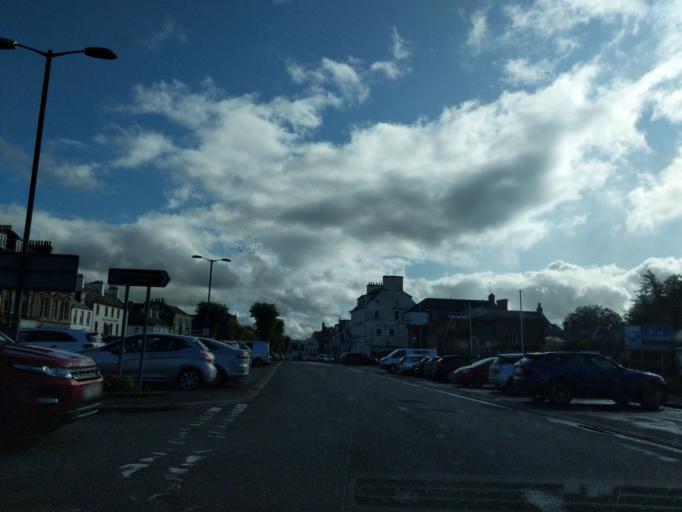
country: GB
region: Scotland
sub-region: Dumfries and Galloway
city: Moffat
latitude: 55.3341
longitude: -3.4453
